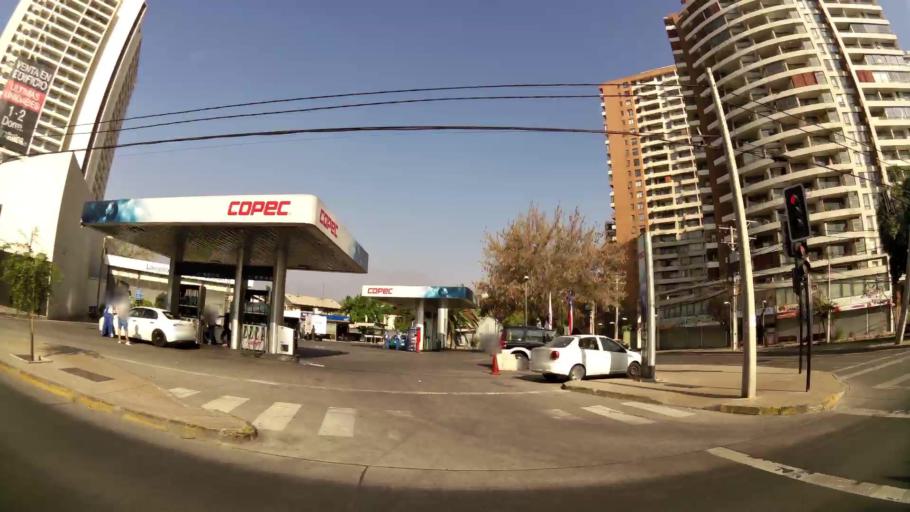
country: CL
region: Santiago Metropolitan
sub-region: Provincia de Santiago
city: Villa Presidente Frei, Nunoa, Santiago, Chile
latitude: -33.4540
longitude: -70.5755
